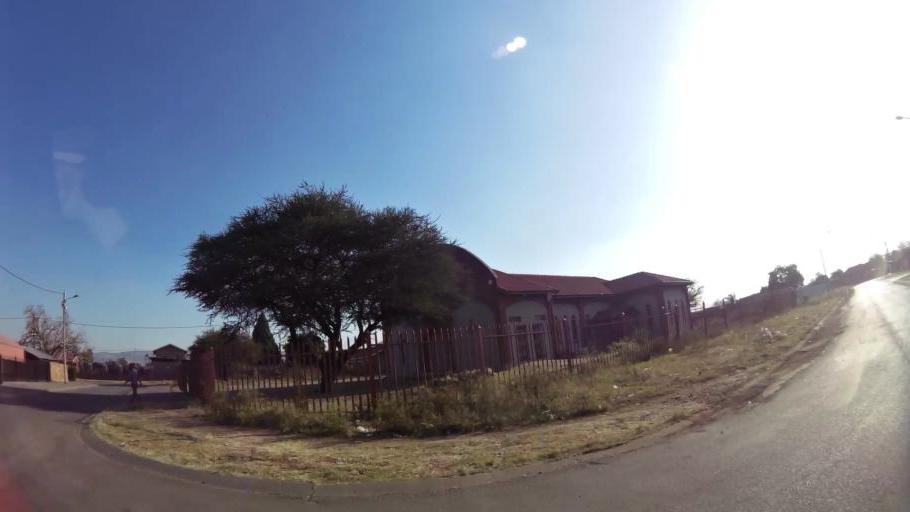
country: ZA
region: North-West
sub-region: Bojanala Platinum District Municipality
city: Rustenburg
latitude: -25.6426
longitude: 27.2378
